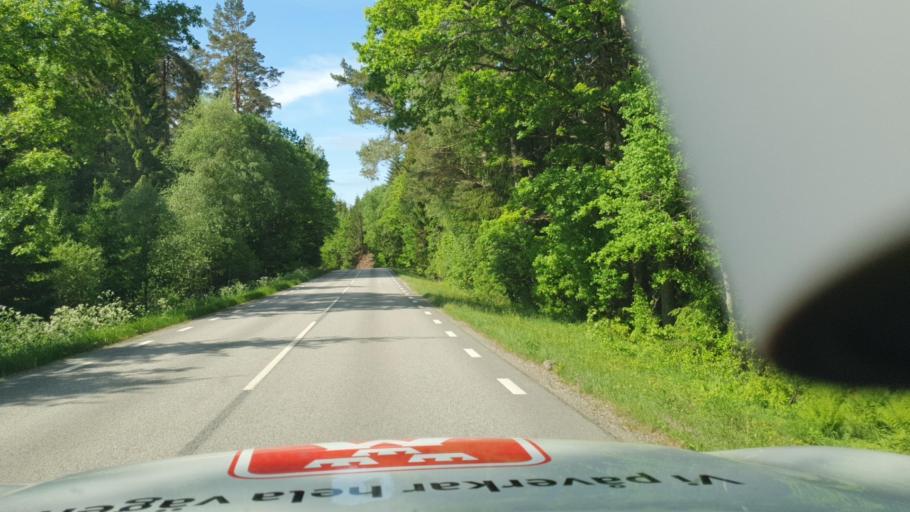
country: SE
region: Vaestra Goetaland
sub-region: Herrljunga Kommun
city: Herrljunga
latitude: 58.0182
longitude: 13.1386
